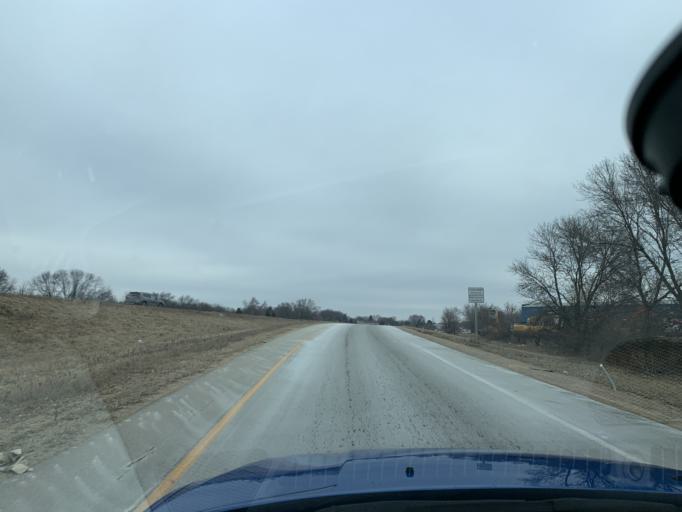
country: US
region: Wisconsin
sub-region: Dane County
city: Sun Prairie
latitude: 43.1767
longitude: -89.2478
